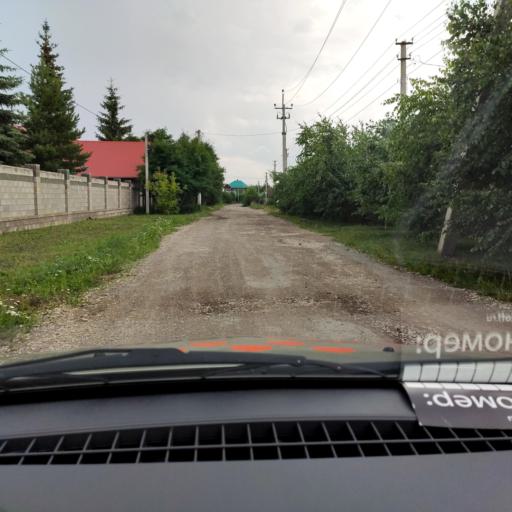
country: RU
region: Bashkortostan
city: Ufa
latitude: 54.6134
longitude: 55.9156
